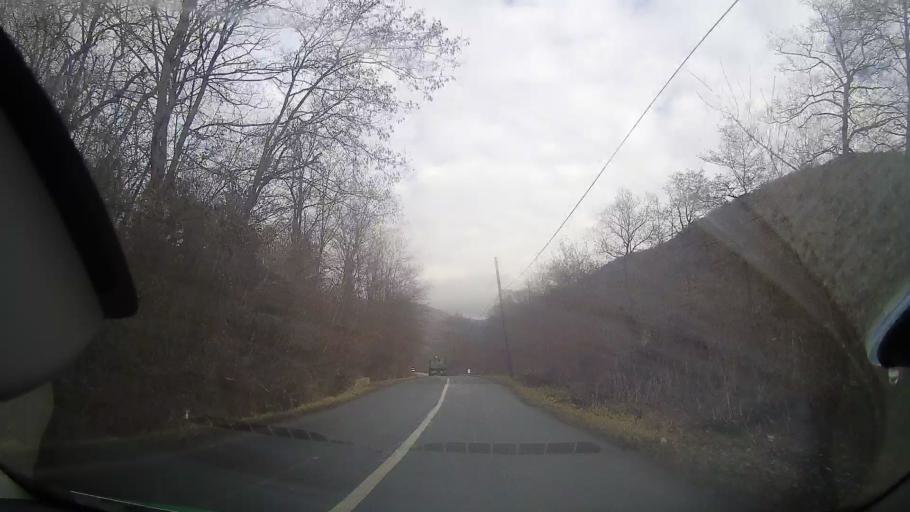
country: RO
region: Alba
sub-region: Comuna Ocolis
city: Ocolis
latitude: 46.4550
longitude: 23.4679
